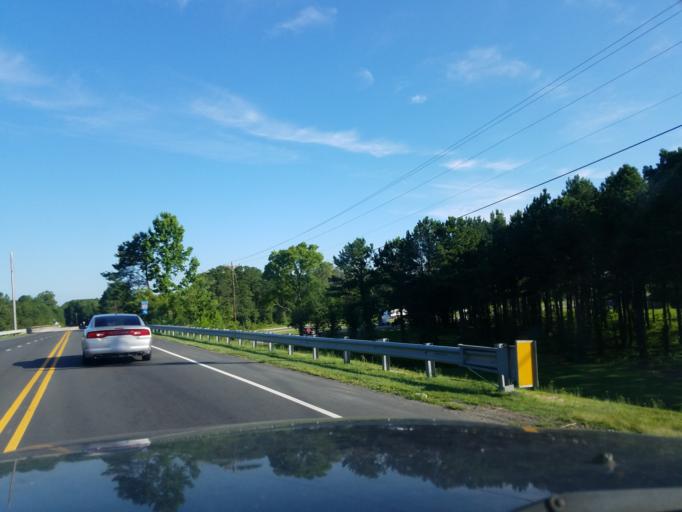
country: US
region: North Carolina
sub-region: Granville County
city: Butner
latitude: 36.1198
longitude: -78.7449
